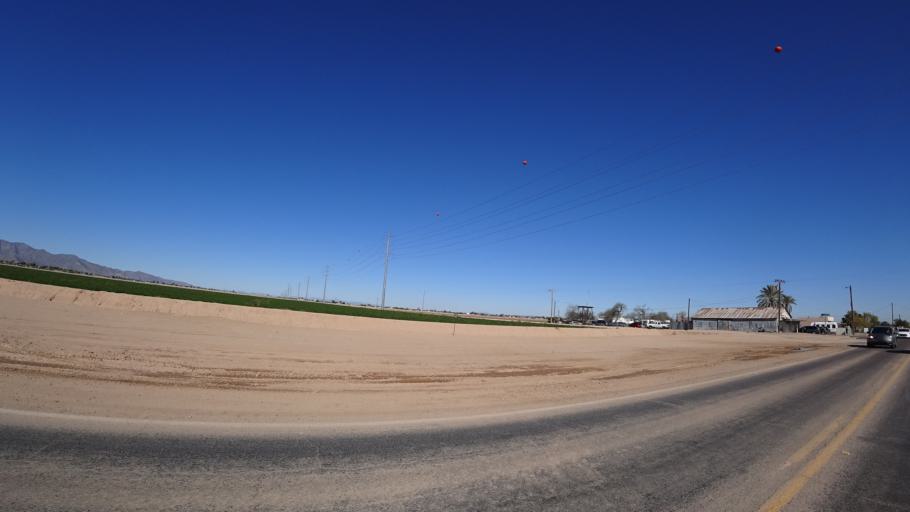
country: US
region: Arizona
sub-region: Maricopa County
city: Goodyear
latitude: 33.4357
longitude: -112.4623
